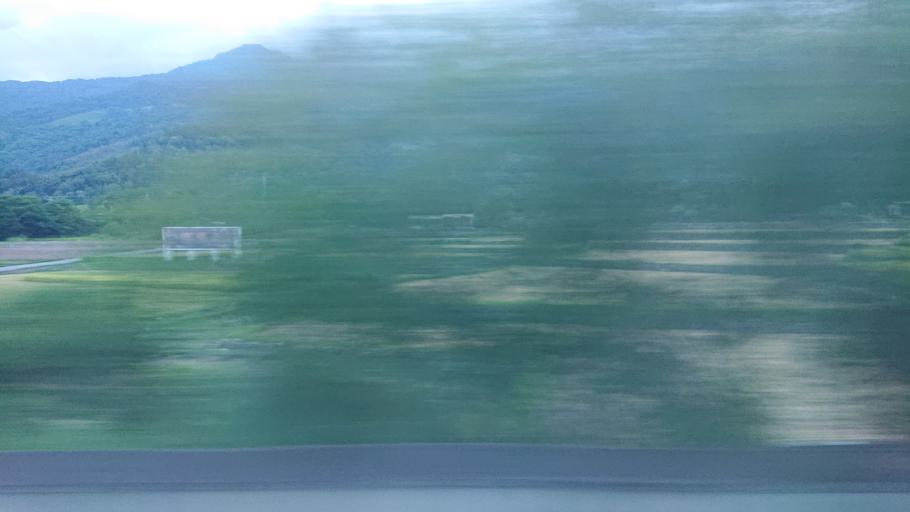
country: TW
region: Taiwan
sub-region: Taitung
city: Taitung
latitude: 23.0312
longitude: 121.1598
